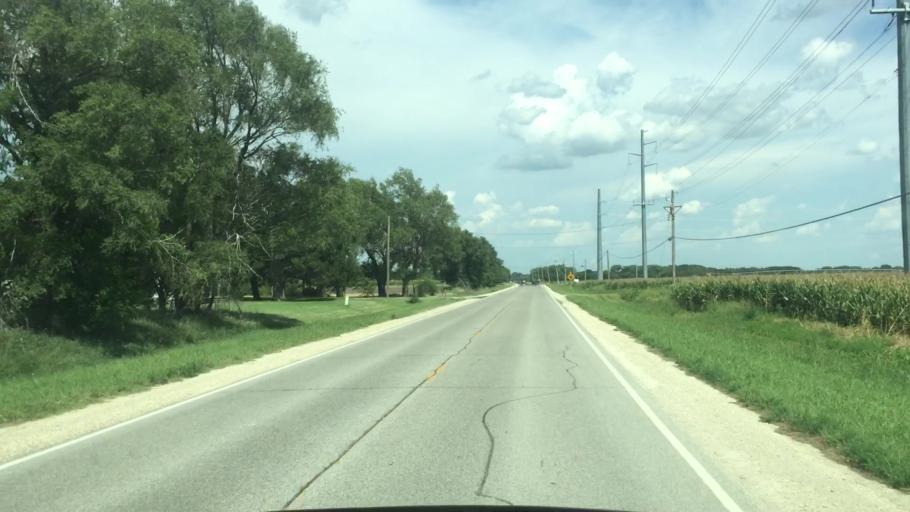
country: US
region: Kansas
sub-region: Sedgwick County
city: Maize
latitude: 37.7810
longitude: -97.4485
